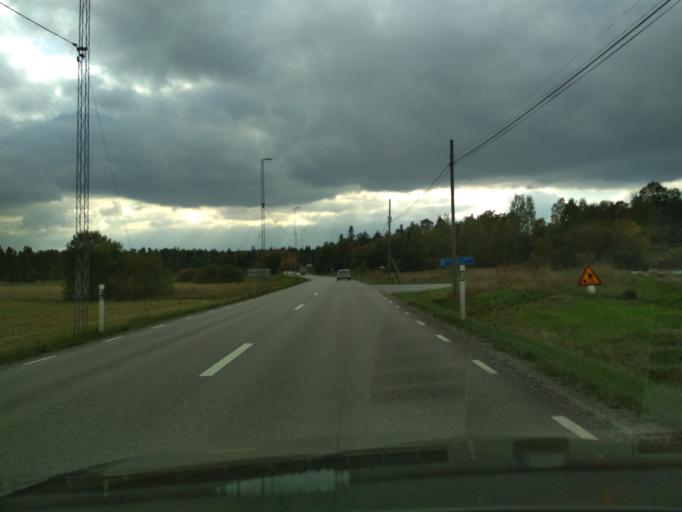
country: SE
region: Stockholm
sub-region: Upplands Vasby Kommun
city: Upplands Vaesby
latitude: 59.5346
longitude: 17.9917
